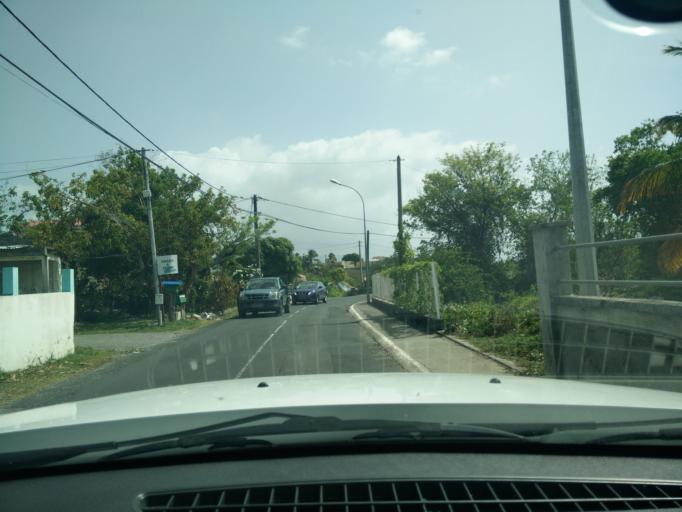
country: GP
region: Guadeloupe
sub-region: Guadeloupe
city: Le Gosier
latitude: 16.2156
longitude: -61.4415
